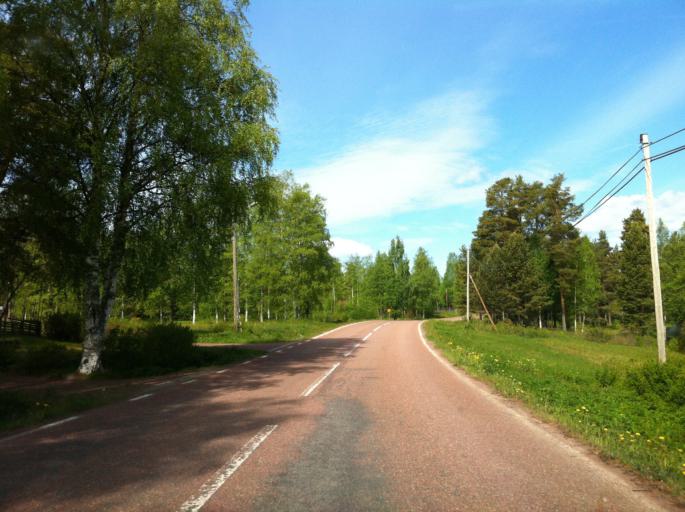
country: SE
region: Dalarna
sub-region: Mora Kommun
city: Mora
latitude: 60.8828
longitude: 14.5699
